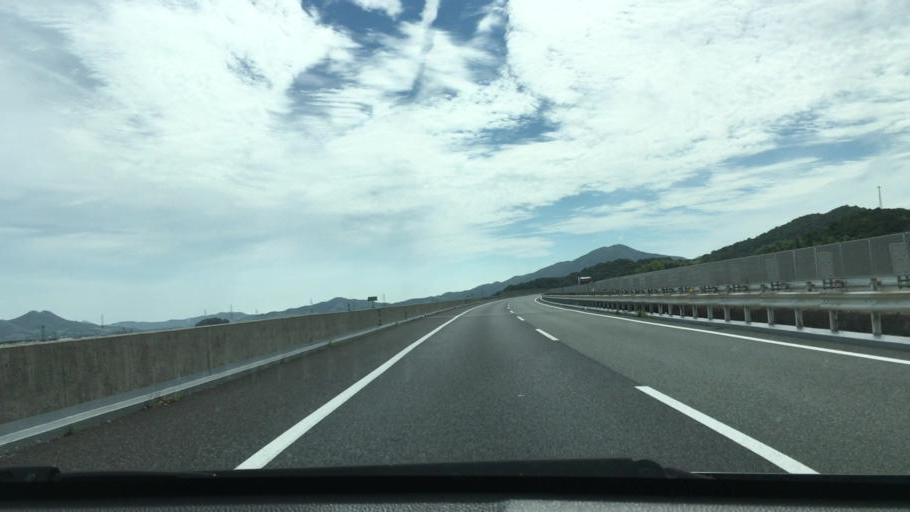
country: JP
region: Yamaguchi
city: Hofu
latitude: 34.0515
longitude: 131.5228
